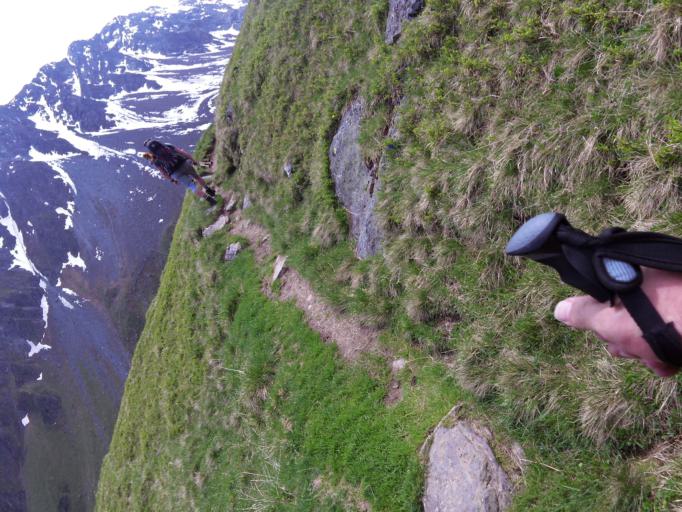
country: AT
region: Tyrol
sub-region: Politischer Bezirk Innsbruck Land
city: Neustift im Stubaital
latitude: 47.0597
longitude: 11.2026
